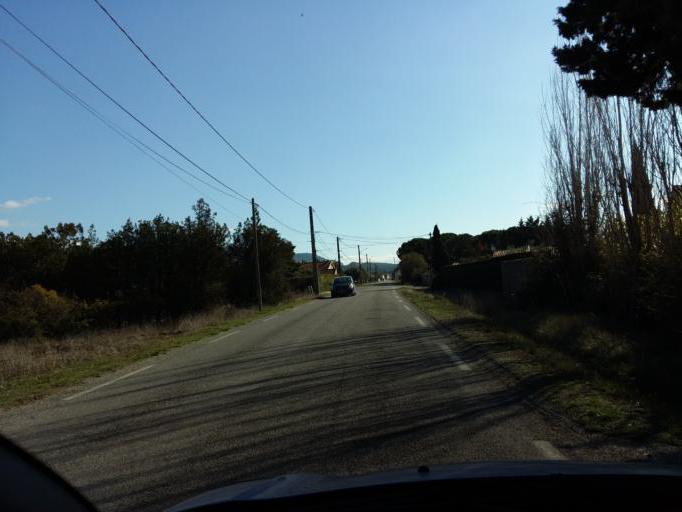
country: FR
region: Provence-Alpes-Cote d'Azur
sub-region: Departement du Vaucluse
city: Cheval-Blanc
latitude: 43.8095
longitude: 5.0645
